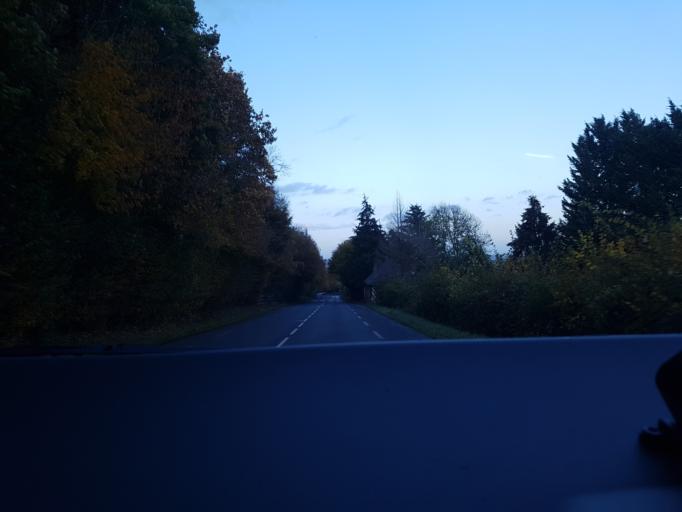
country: FR
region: Lower Normandy
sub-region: Departement du Calvados
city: Saint-Gatien-des-Bois
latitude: 49.2680
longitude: 0.1630
